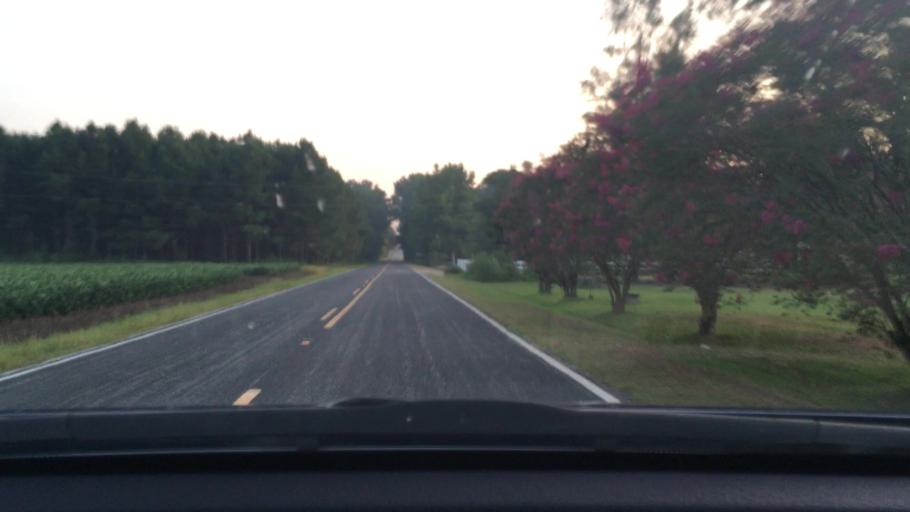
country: US
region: South Carolina
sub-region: Lee County
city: Bishopville
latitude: 34.2117
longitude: -80.1353
